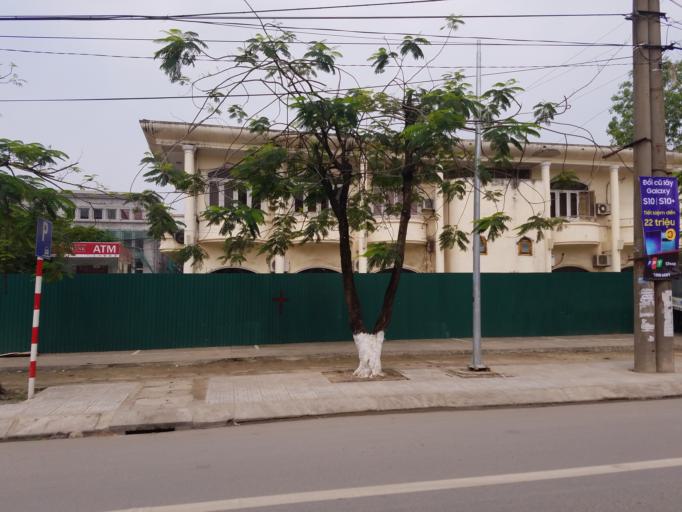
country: VN
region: Thai Nguyen
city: Thanh Pho Thai Nguyen
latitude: 21.5870
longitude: 105.8307
